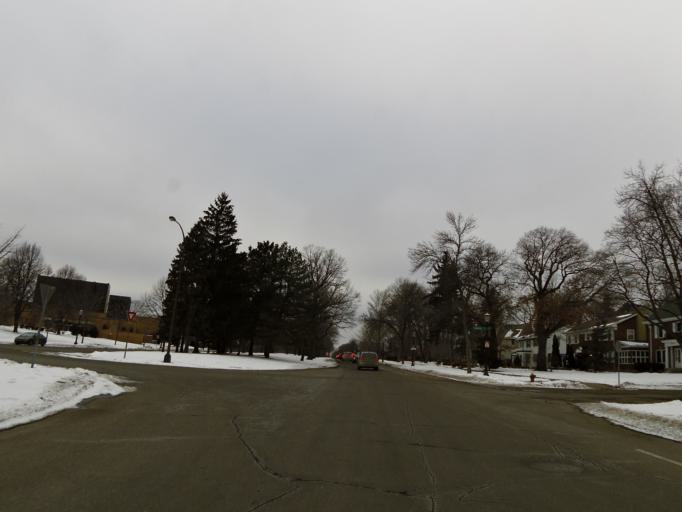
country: US
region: Minnesota
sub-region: Ramsey County
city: Falcon Heights
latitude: 44.9415
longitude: -93.1539
